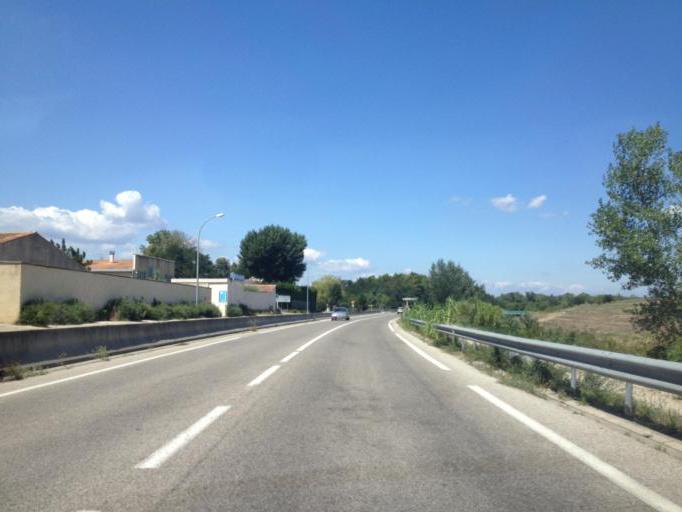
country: FR
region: Languedoc-Roussillon
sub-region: Departement du Gard
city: Roquemaure
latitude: 44.0514
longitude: 4.7847
